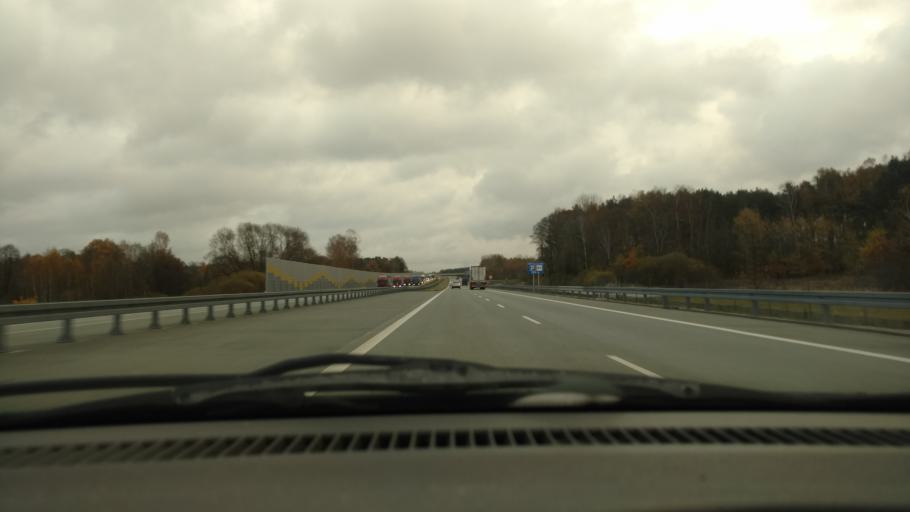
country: PL
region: Lodz Voivodeship
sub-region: Powiat pabianicki
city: Ksawerow
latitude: 51.6316
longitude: 19.4217
